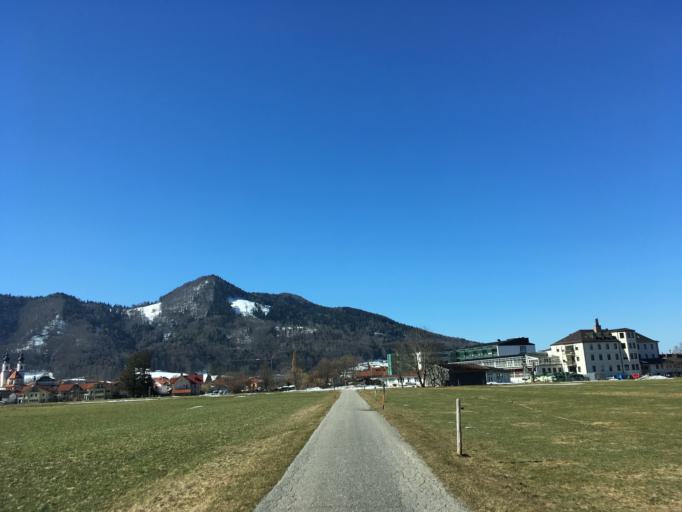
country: DE
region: Bavaria
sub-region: Upper Bavaria
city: Aschau im Chiemgau
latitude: 47.7816
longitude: 12.3313
